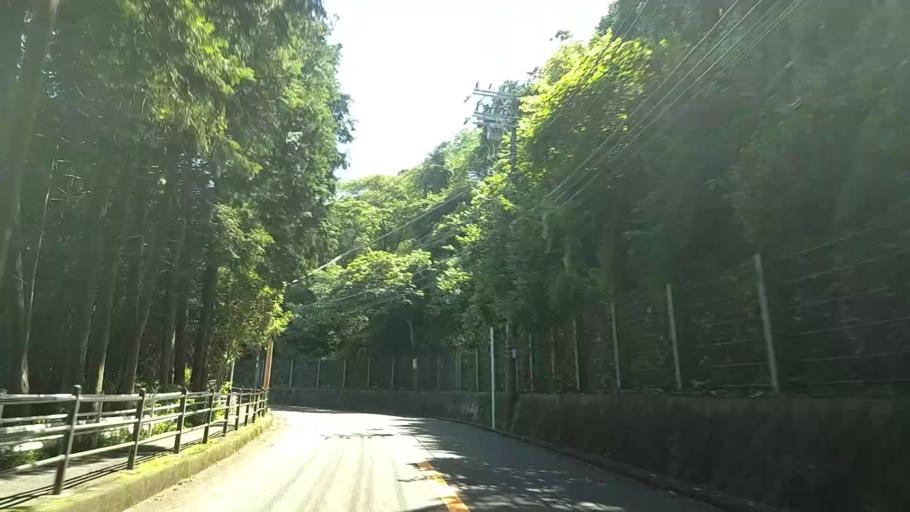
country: JP
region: Kanagawa
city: Zushi
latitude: 35.2930
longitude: 139.5897
